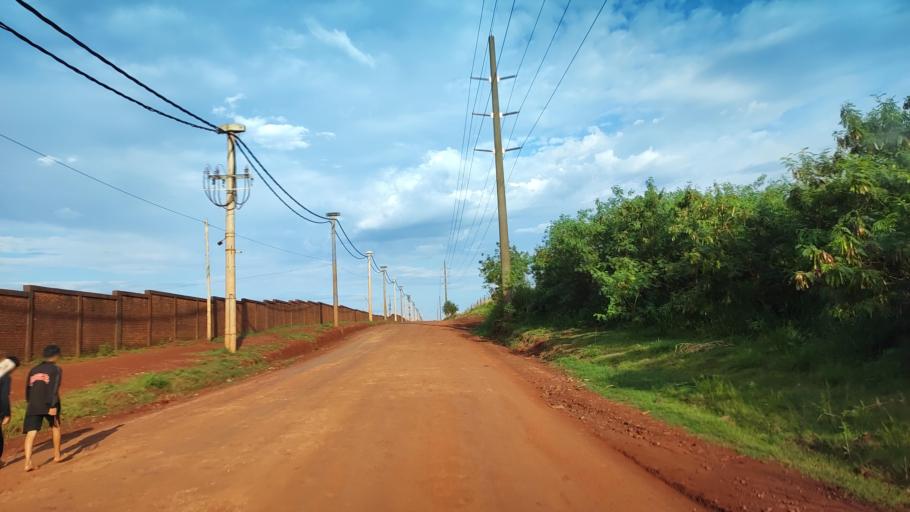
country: AR
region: Misiones
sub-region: Departamento de Capital
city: Posadas
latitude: -27.4437
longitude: -55.9291
